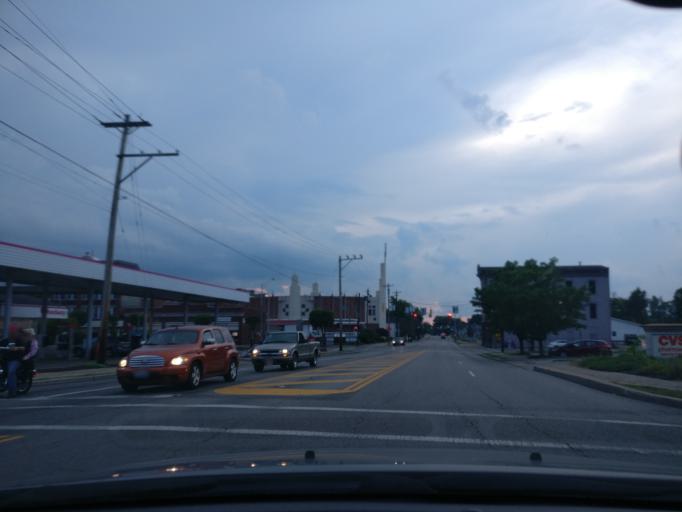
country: US
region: Ohio
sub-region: Warren County
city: Franklin
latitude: 39.5618
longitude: -84.3018
